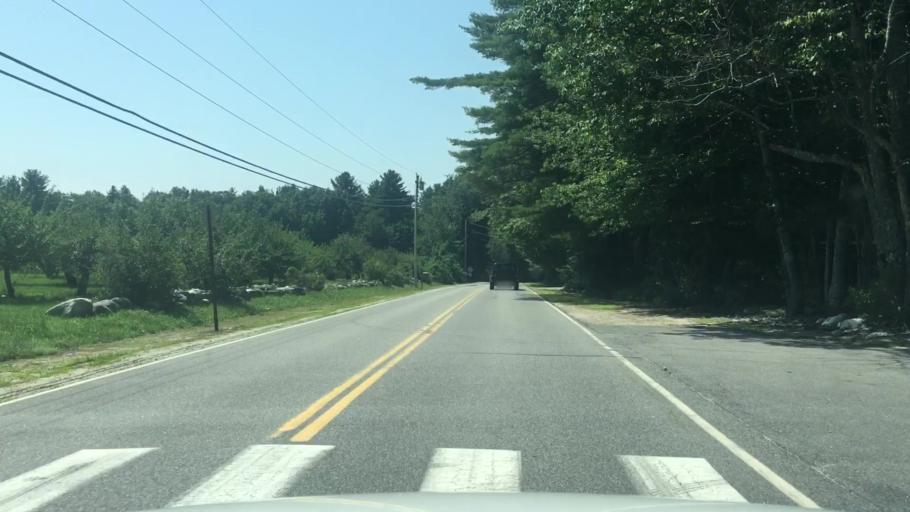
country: US
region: Maine
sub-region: Cumberland County
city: Cumberland Center
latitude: 43.8288
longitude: -70.2988
